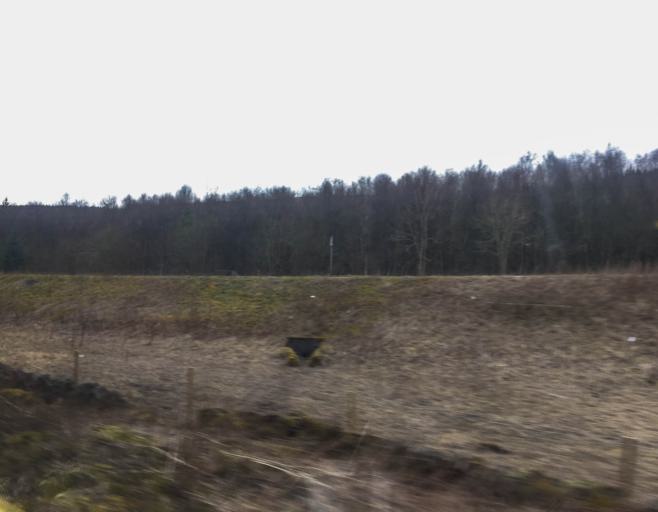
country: GB
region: Scotland
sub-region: Dumfries and Galloway
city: Moffat
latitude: 55.4272
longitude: -3.6146
